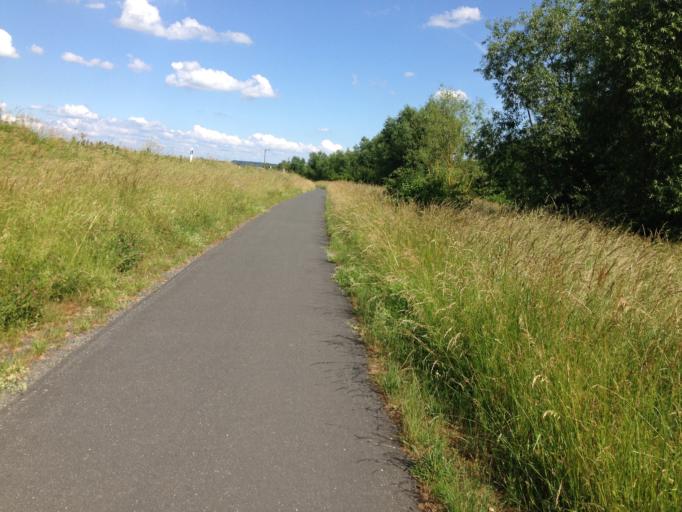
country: DE
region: Hesse
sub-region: Regierungsbezirk Giessen
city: Hoernsheim
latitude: 50.5174
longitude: 8.5956
